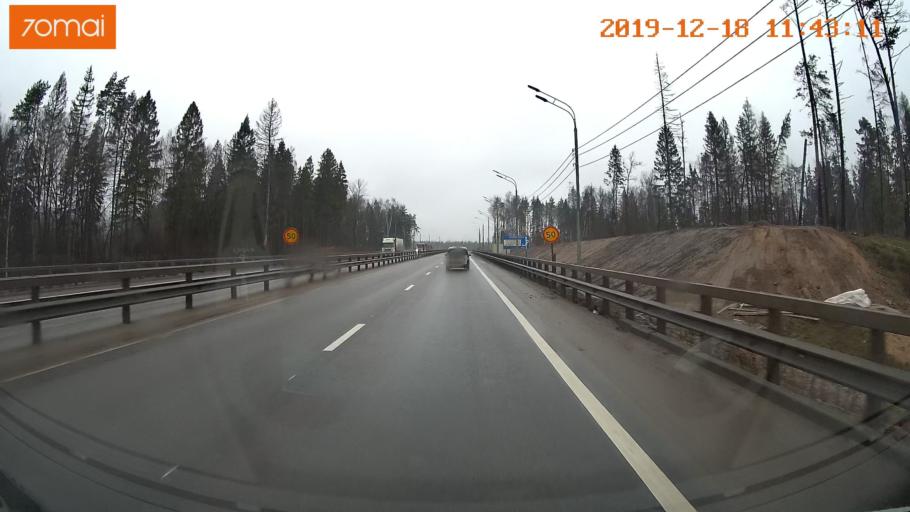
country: RU
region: Moskovskaya
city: Zvenigorod
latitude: 55.7318
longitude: 36.8791
